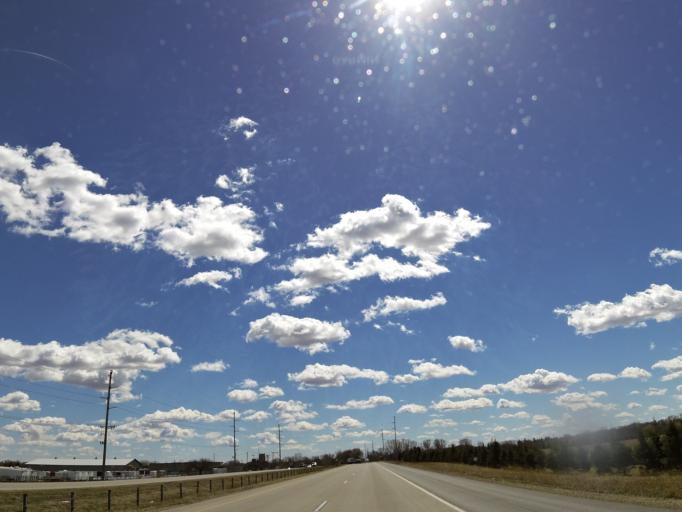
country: US
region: Minnesota
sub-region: Dakota County
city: Hastings
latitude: 44.7740
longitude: -92.8632
